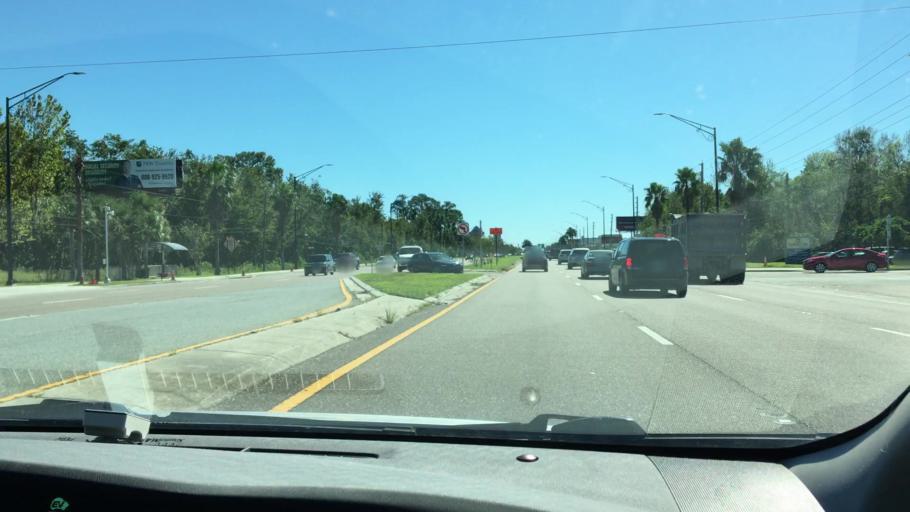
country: US
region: Florida
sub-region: Orange County
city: Conway
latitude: 28.4792
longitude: -81.3102
